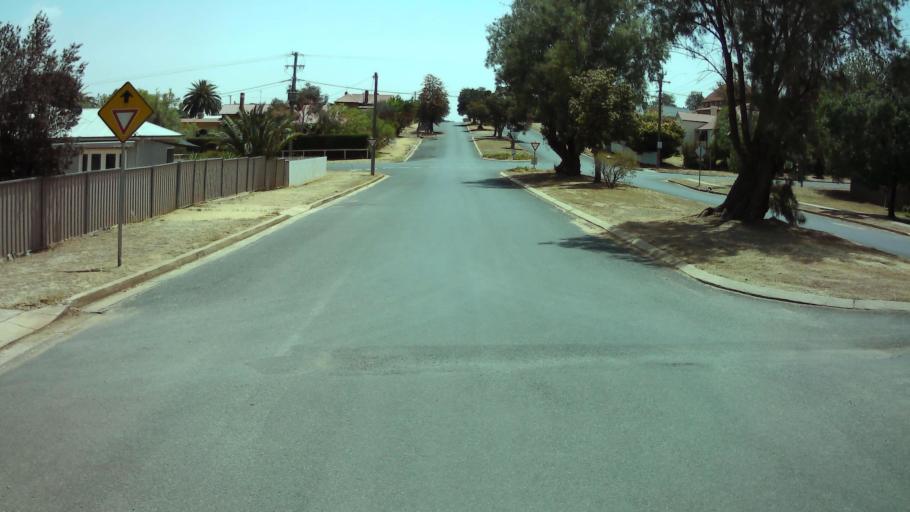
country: AU
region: New South Wales
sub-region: Weddin
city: Grenfell
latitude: -33.8980
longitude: 148.1596
